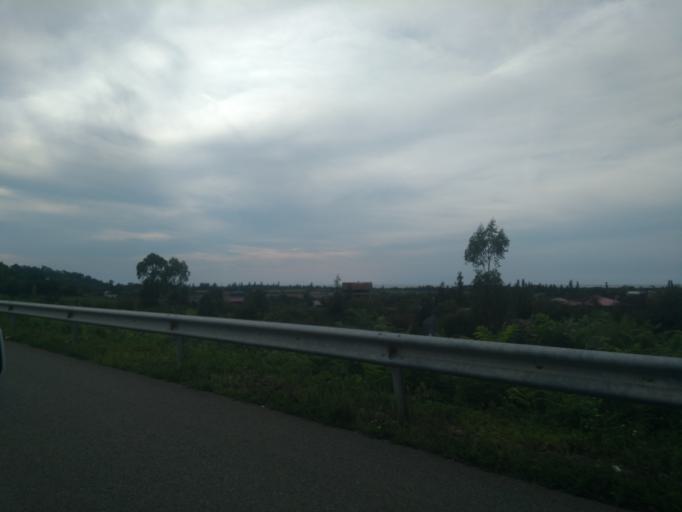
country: GE
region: Ajaria
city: Kobuleti
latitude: 41.7924
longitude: 41.7900
